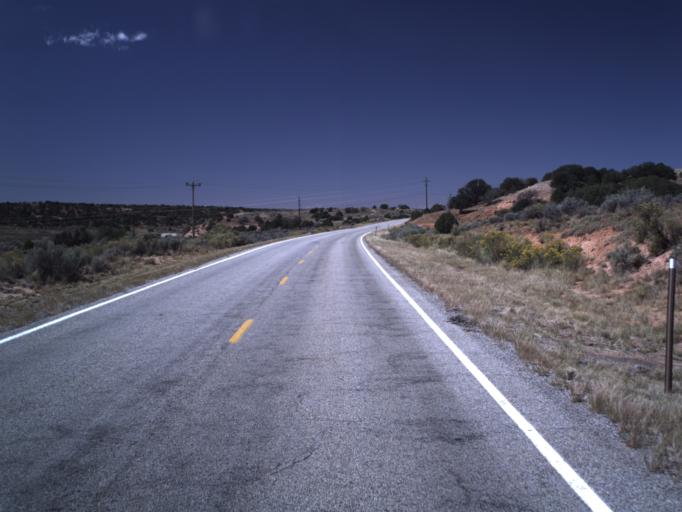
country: US
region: Utah
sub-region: Grand County
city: Moab
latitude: 38.3049
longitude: -109.3892
